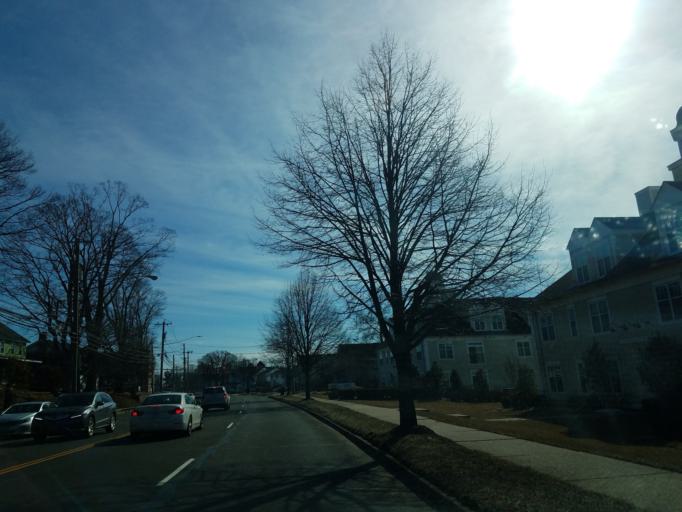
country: US
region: Connecticut
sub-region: Fairfield County
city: Norwalk
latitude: 41.1120
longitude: -73.4078
